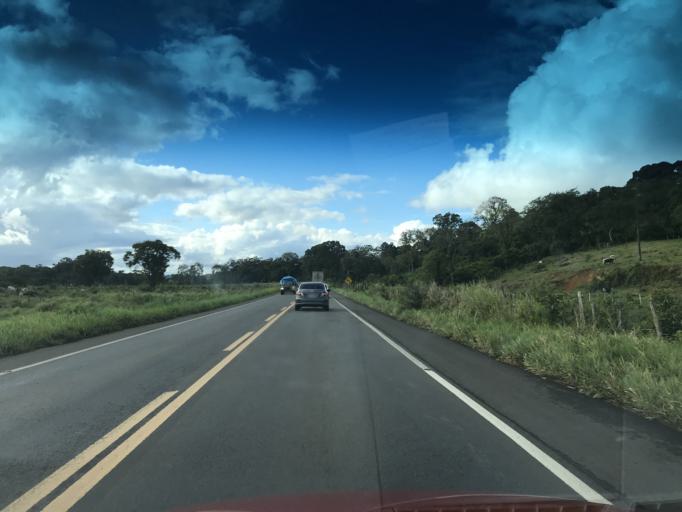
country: BR
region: Bahia
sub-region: Ibirapitanga
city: Ibirapitanga
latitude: -14.1584
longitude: -39.3274
